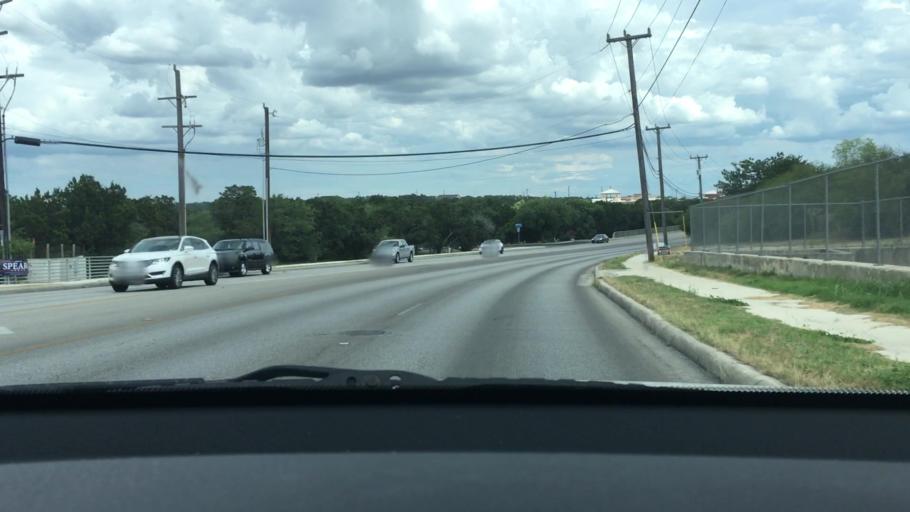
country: US
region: Texas
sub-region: Bexar County
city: Timberwood Park
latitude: 29.6524
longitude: -98.4265
